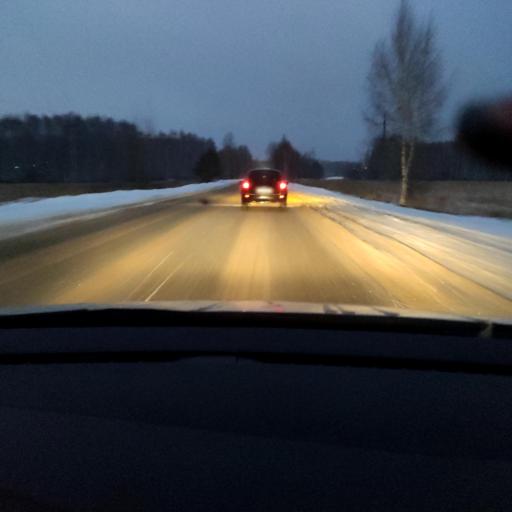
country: RU
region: Tatarstan
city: Aysha
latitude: 55.8676
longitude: 48.5814
